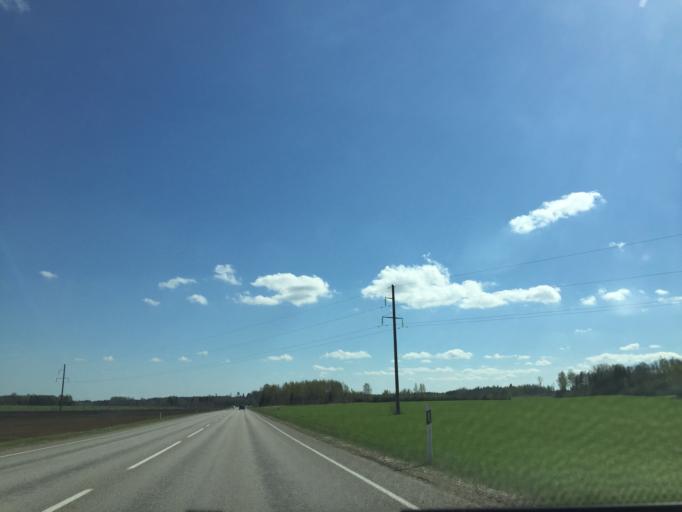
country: EE
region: Valgamaa
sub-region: Valga linn
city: Valga
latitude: 57.8812
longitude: 26.0594
